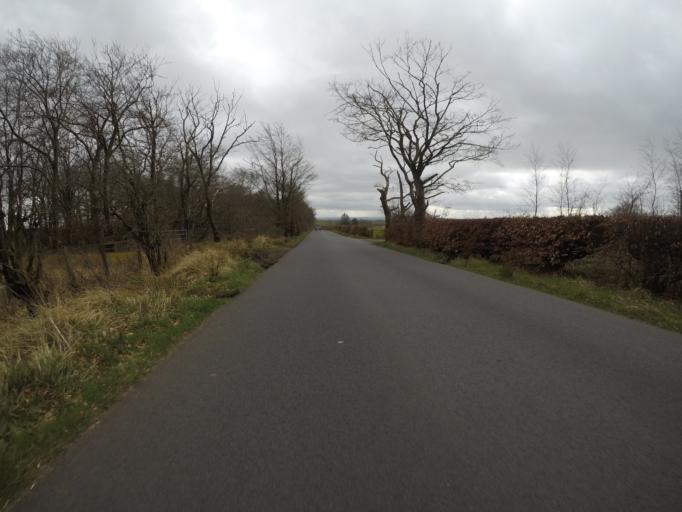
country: GB
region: Scotland
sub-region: East Ayrshire
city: Stewarton
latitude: 55.6773
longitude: -4.4407
